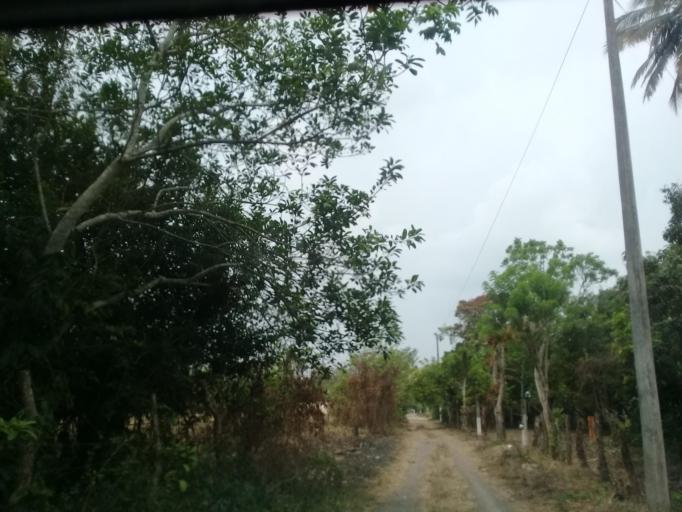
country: MX
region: Veracruz
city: Jamapa
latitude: 19.0505
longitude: -96.2026
